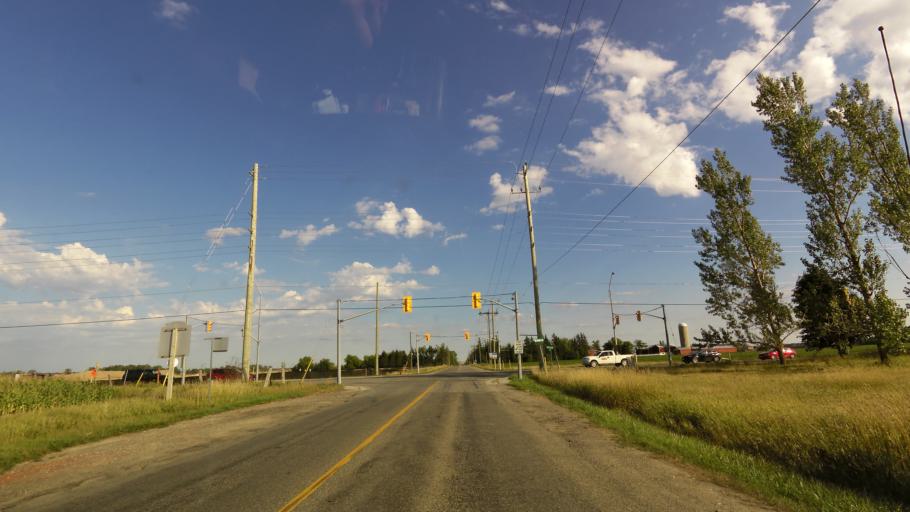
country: CA
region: Ontario
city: Brampton
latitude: 43.7143
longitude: -79.8466
